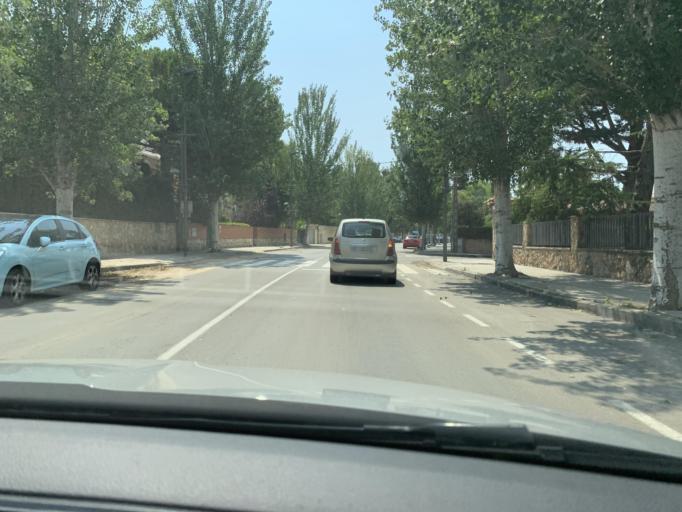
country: ES
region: Catalonia
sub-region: Provincia de Tarragona
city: Altafulla
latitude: 41.1335
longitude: 1.3458
